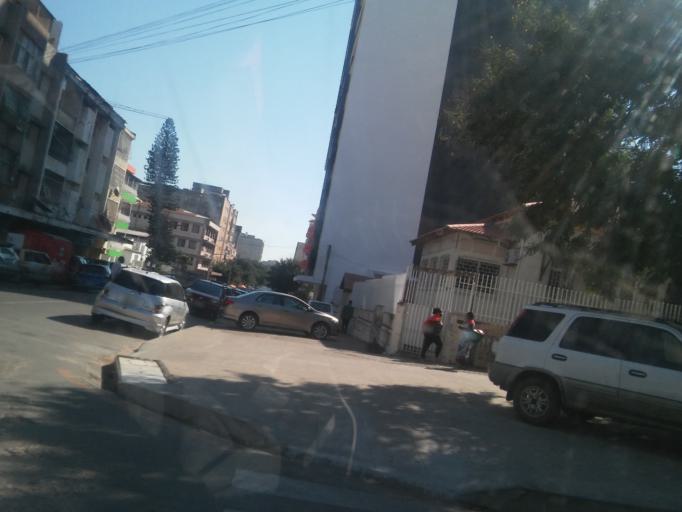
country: MZ
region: Maputo City
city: Maputo
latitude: -25.9637
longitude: 32.5726
